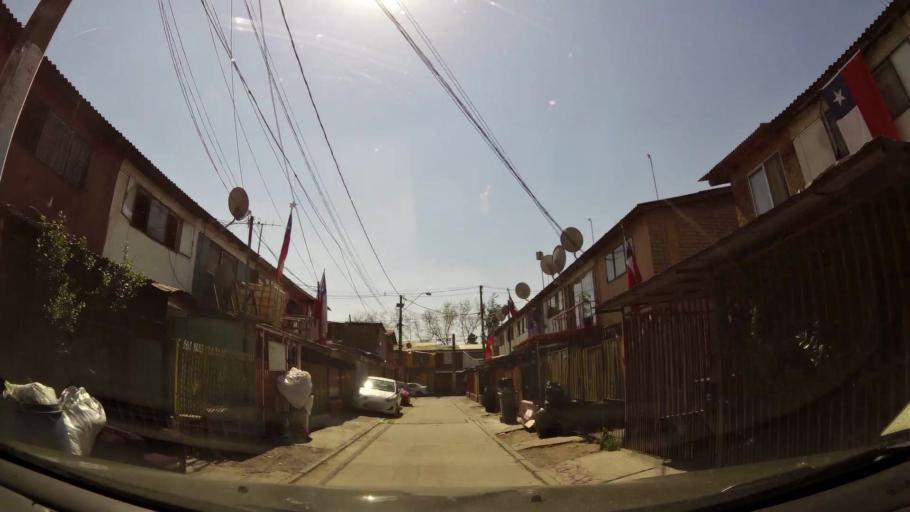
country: CL
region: Santiago Metropolitan
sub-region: Provincia de Santiago
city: La Pintana
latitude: -33.5925
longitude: -70.6194
